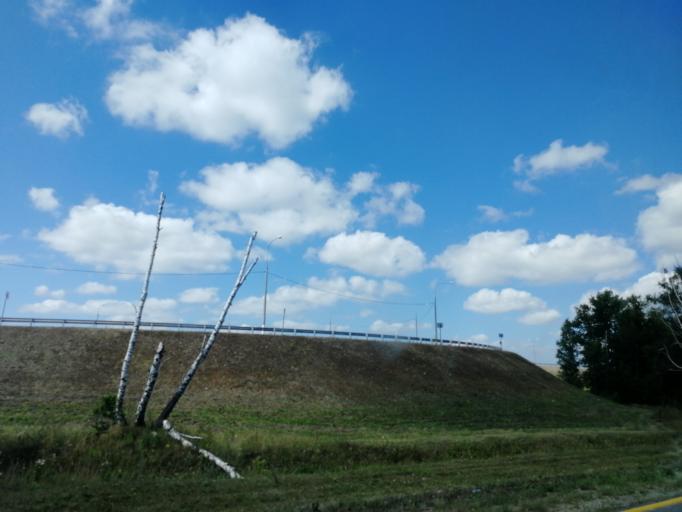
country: RU
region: Tula
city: Dubovka
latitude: 53.8894
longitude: 38.0565
